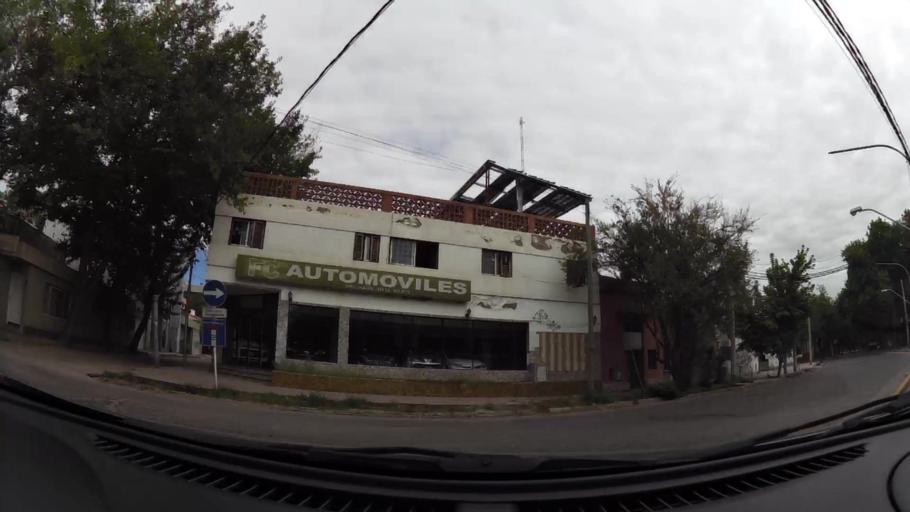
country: AR
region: Mendoza
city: Mendoza
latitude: -32.8979
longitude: -68.8512
